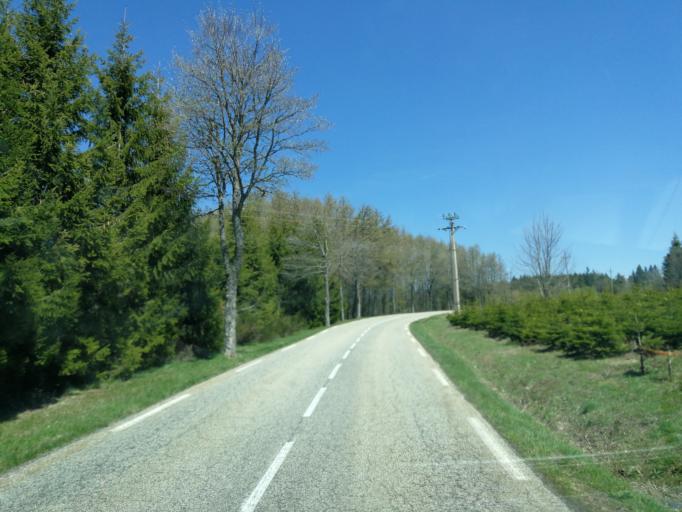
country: FR
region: Rhone-Alpes
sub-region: Departement de l'Ardeche
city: Saint-Agreve
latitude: 45.0709
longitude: 4.3834
